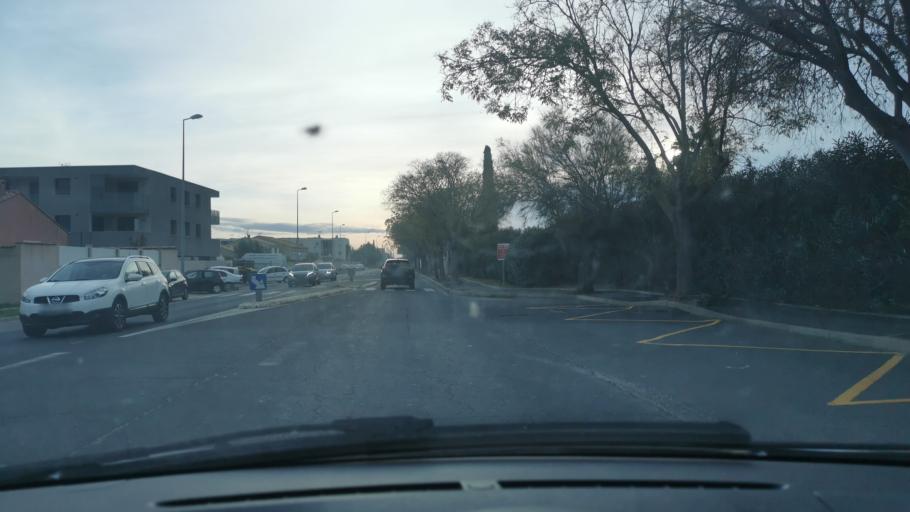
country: FR
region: Languedoc-Roussillon
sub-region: Departement de l'Herault
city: Frontignan
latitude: 43.4602
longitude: 3.7647
